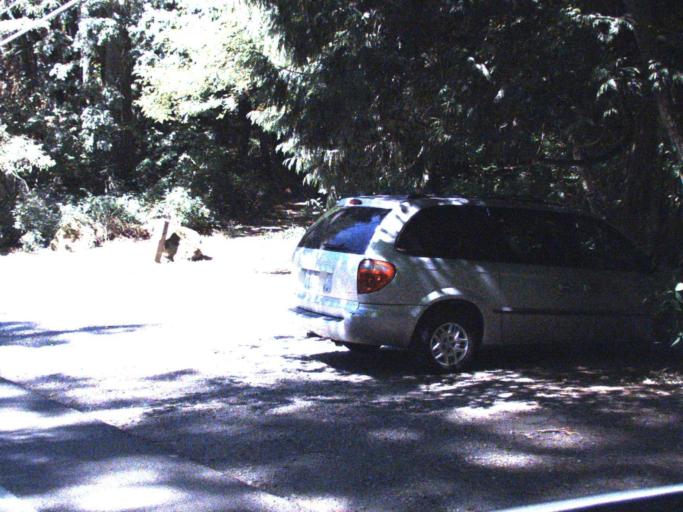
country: US
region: Washington
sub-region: King County
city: East Renton Highlands
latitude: 47.5133
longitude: -122.0780
